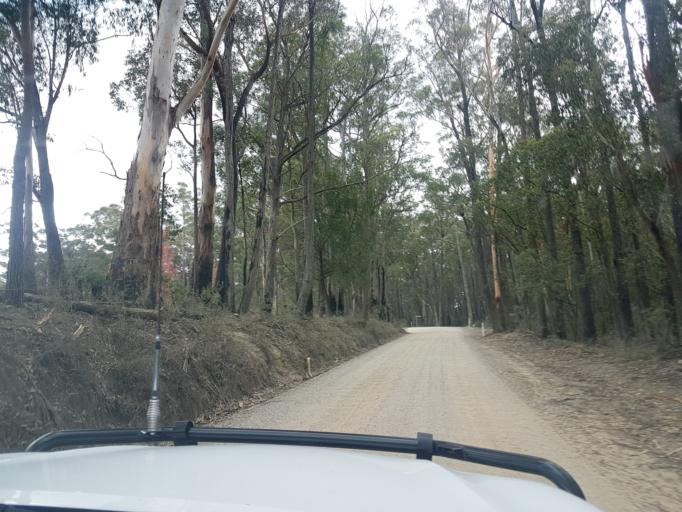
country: AU
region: Victoria
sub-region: East Gippsland
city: Bairnsdale
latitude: -37.6908
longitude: 147.5643
